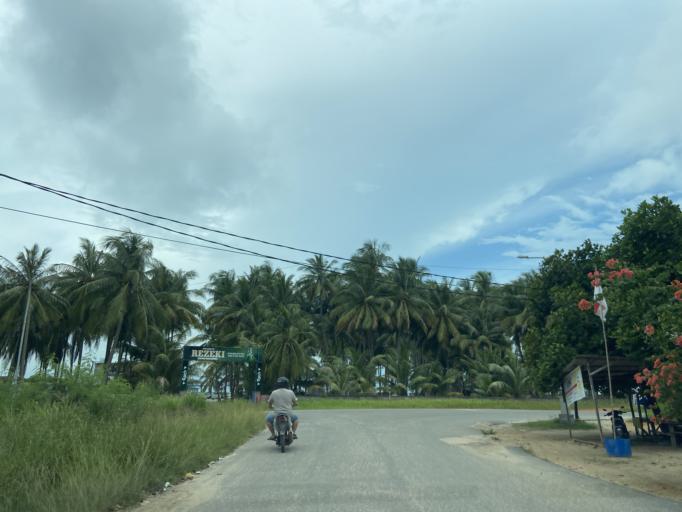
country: SG
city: Singapore
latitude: 1.1532
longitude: 104.1389
